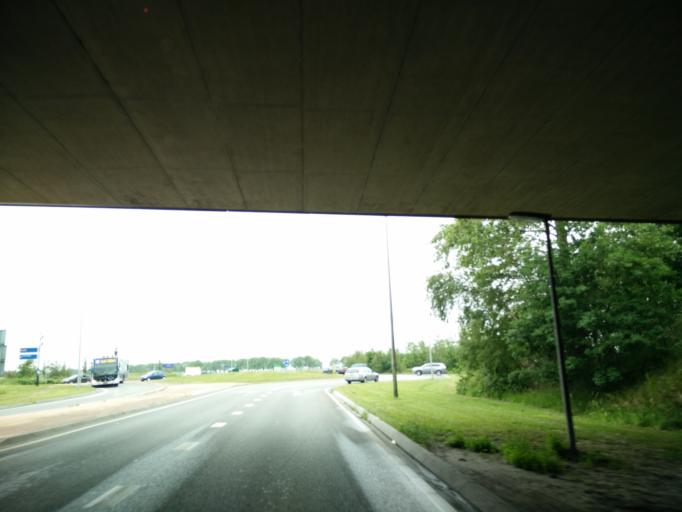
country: NL
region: Groningen
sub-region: Gemeente Groningen
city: Groningen
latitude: 53.2002
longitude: 6.5104
